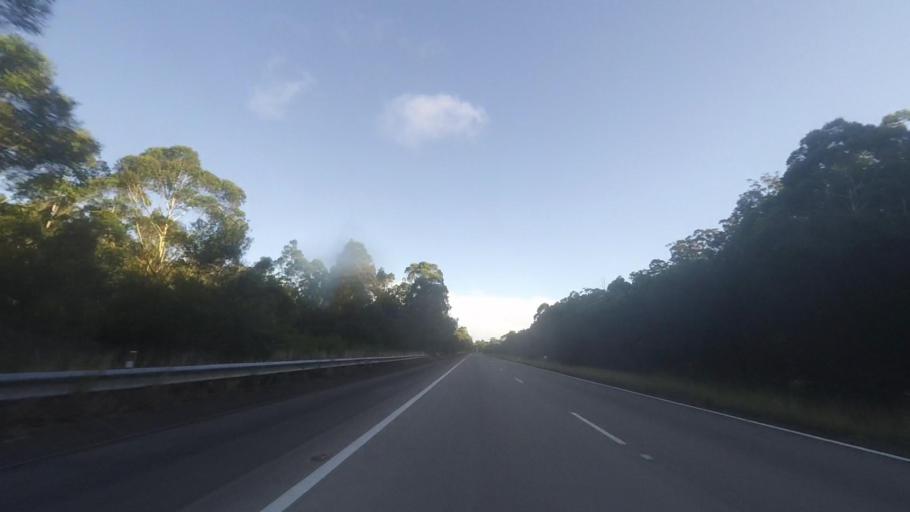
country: AU
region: New South Wales
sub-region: Great Lakes
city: Bulahdelah
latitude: -32.2947
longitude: 152.3443
